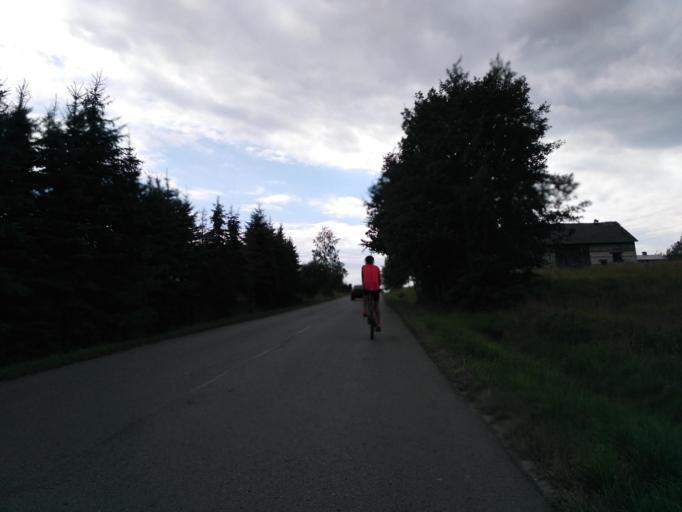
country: PL
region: Subcarpathian Voivodeship
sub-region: Powiat rzeszowski
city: Lecka
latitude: 49.9135
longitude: 22.0238
